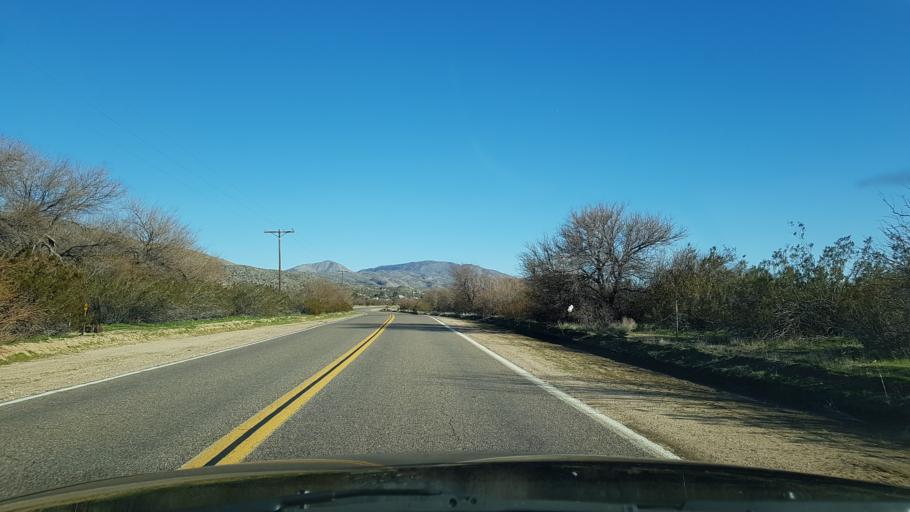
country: US
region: California
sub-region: San Diego County
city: Julian
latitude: 33.0907
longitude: -116.4545
